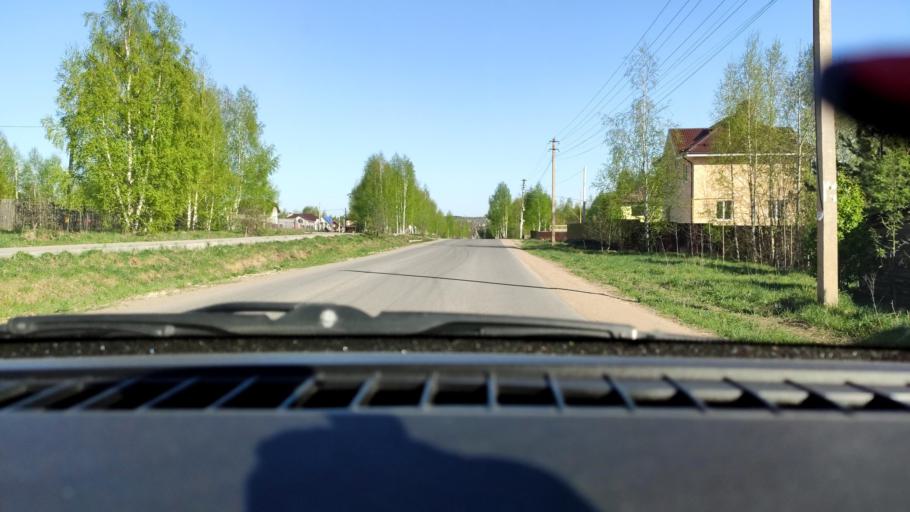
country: RU
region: Perm
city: Kondratovo
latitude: 58.0570
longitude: 56.0097
